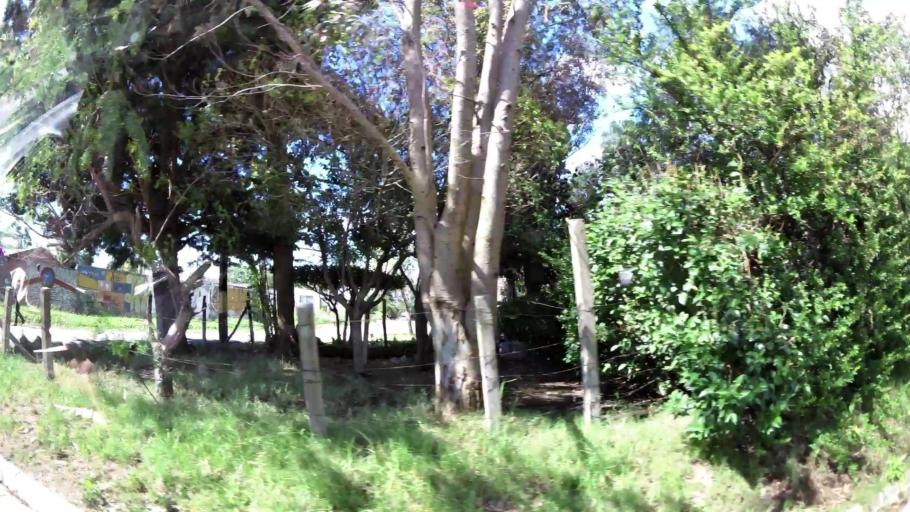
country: UY
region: Montevideo
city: Montevideo
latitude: -34.8424
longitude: -56.1895
